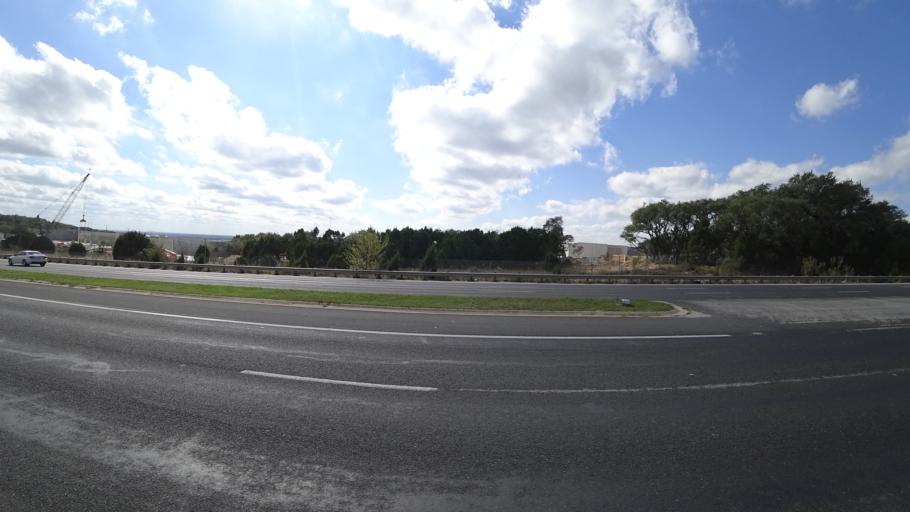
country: US
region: Texas
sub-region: Travis County
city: Barton Creek
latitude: 30.2563
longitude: -97.8675
